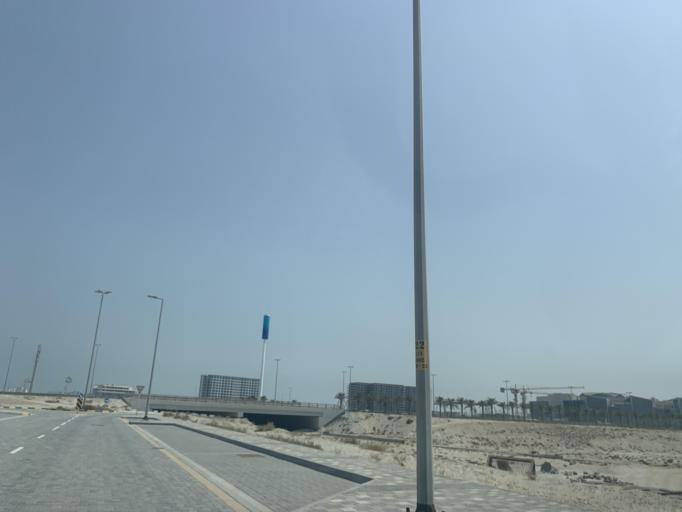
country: BH
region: Muharraq
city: Al Hadd
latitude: 26.2762
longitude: 50.6751
